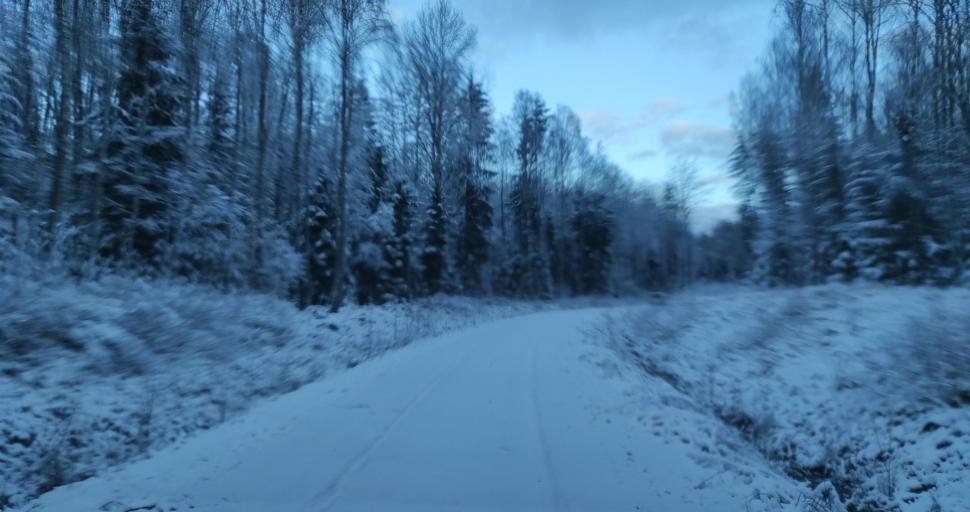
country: LV
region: Skrunda
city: Skrunda
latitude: 56.5846
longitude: 21.9183
